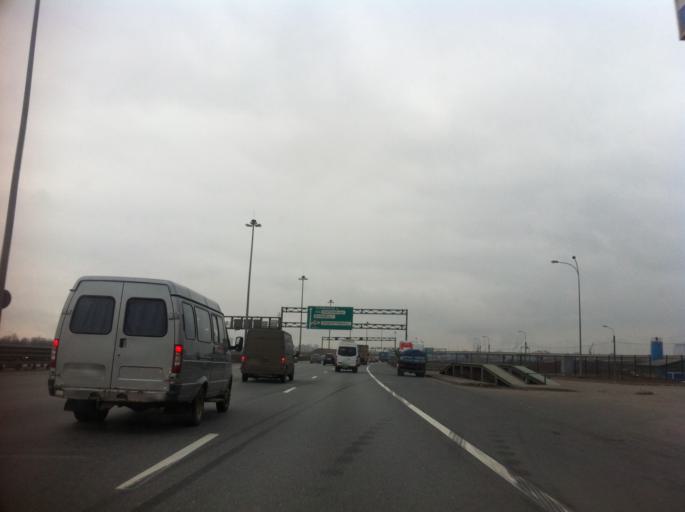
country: RU
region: St.-Petersburg
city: Dachnoye
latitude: 59.8261
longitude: 30.2931
